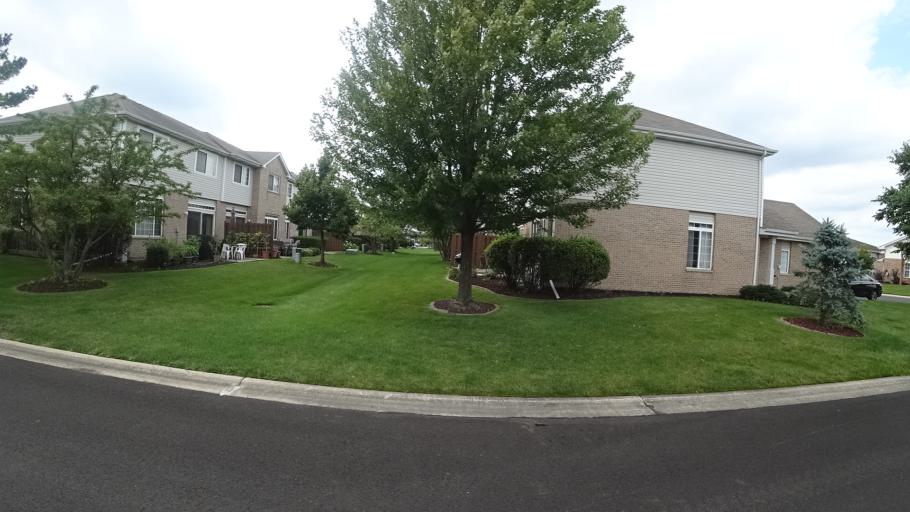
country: US
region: Illinois
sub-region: Cook County
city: Orland Hills
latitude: 41.5610
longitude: -87.8232
